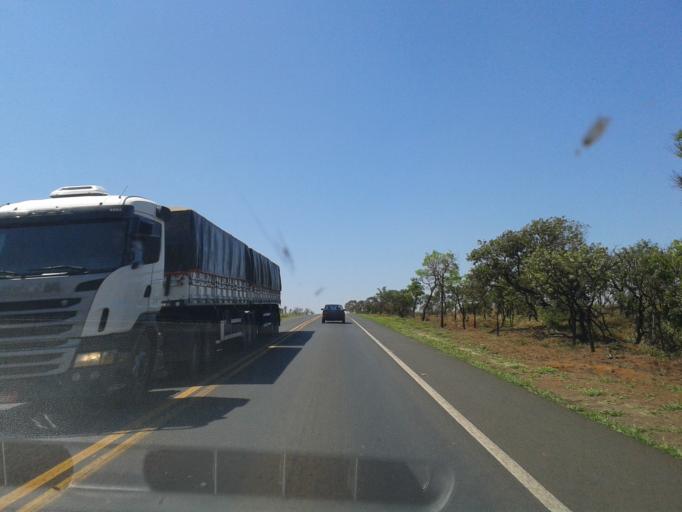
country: BR
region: Minas Gerais
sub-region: Uberaba
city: Uberaba
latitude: -19.3009
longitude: -47.5898
